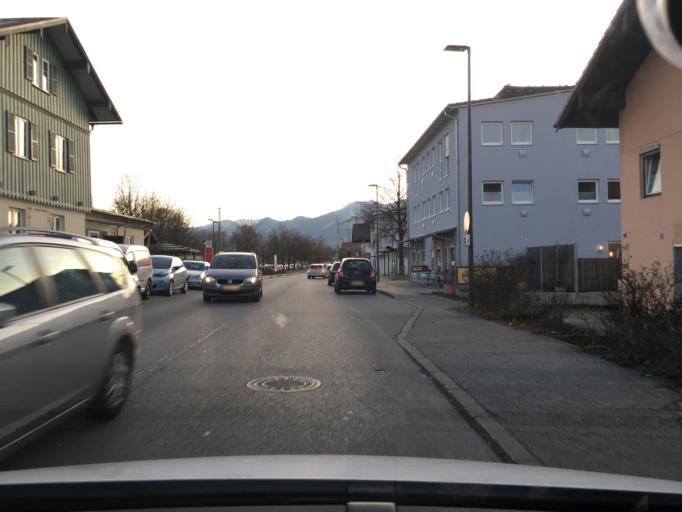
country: DE
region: Bavaria
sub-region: Upper Bavaria
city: Raubling
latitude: 47.7888
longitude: 12.1098
